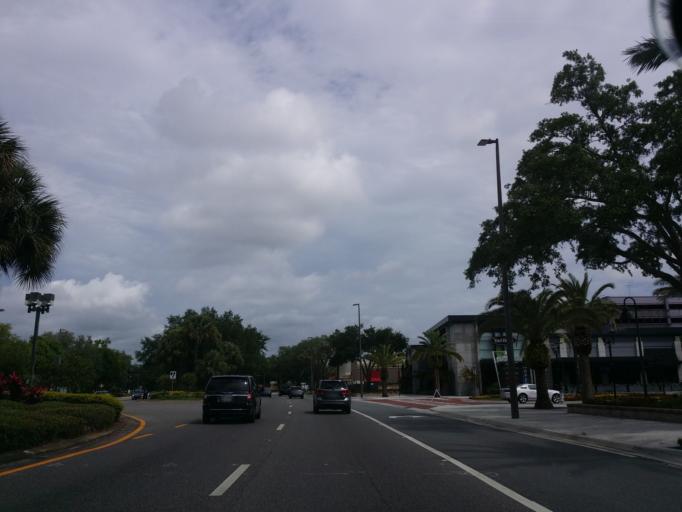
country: US
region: Florida
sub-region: Orange County
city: Doctor Phillips
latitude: 28.4427
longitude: -81.4702
